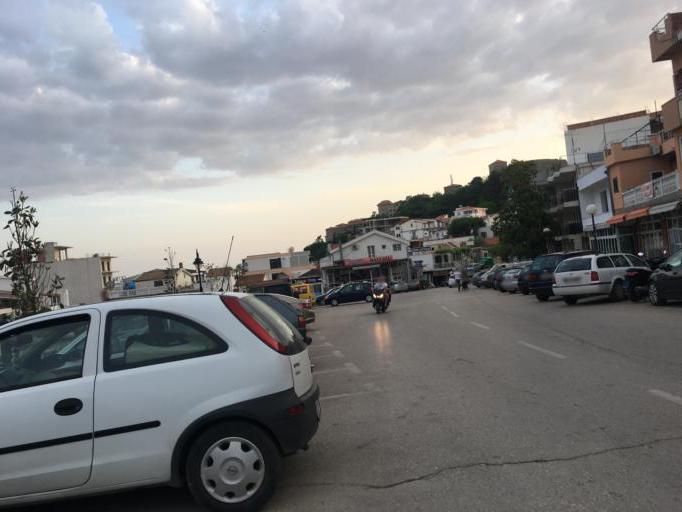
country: ME
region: Ulcinj
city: Ulcinj
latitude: 41.9264
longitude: 19.2050
